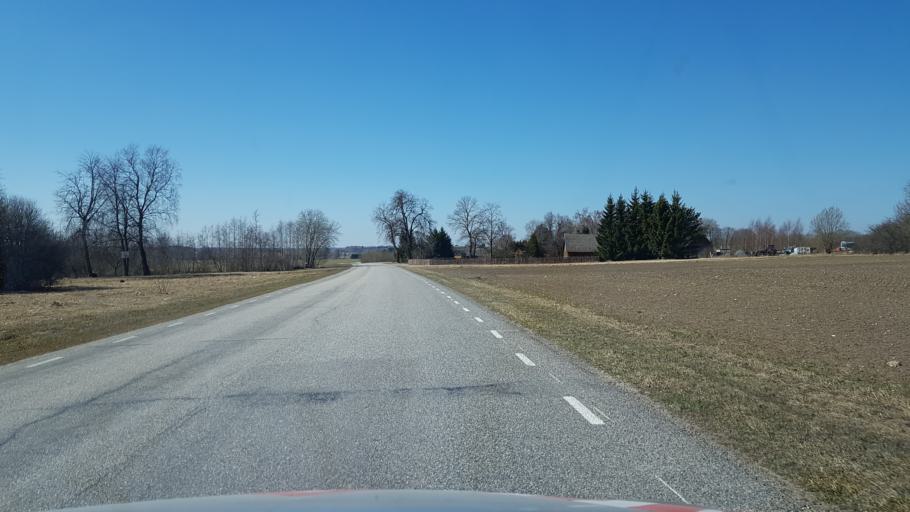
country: EE
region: Laeaene-Virumaa
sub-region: Vinni vald
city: Vinni
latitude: 59.0697
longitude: 26.5141
